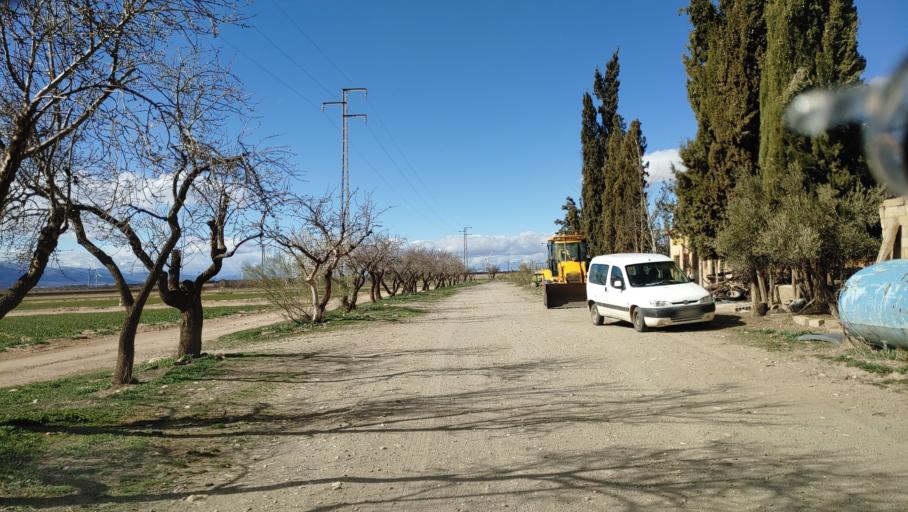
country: ES
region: Andalusia
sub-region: Provincia de Granada
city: Hueneja
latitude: 37.2214
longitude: -2.9502
